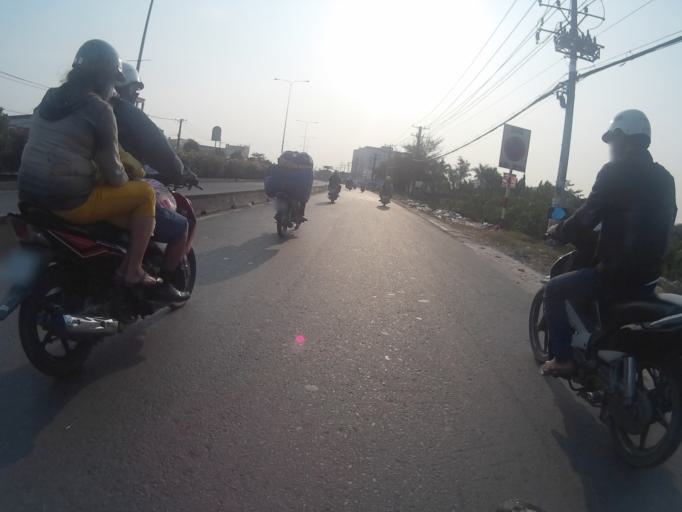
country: VN
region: Ho Chi Minh City
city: Ho Chi Minh City
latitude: 10.8473
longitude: 106.6207
